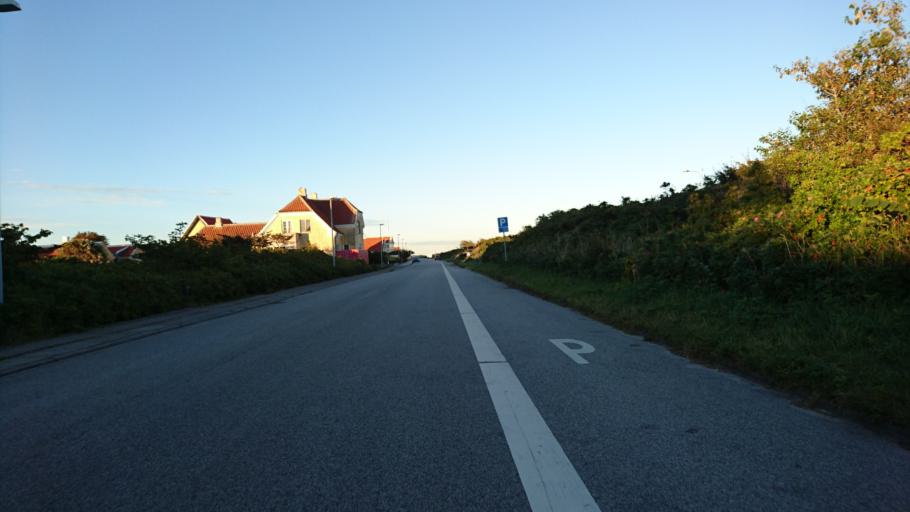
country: DK
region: North Denmark
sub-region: Frederikshavn Kommune
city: Skagen
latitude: 57.7231
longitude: 10.5985
